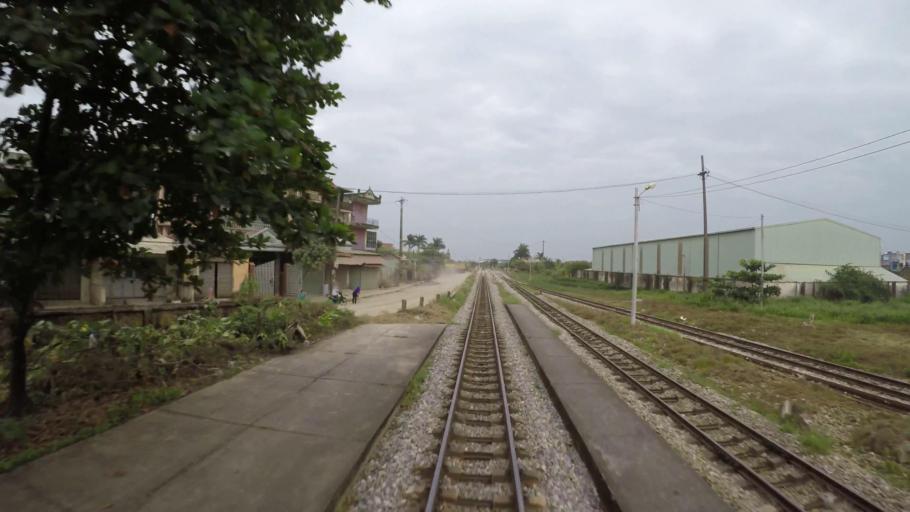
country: VN
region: Hai Duong
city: Lai Cach
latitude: 20.9488
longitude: 106.2517
